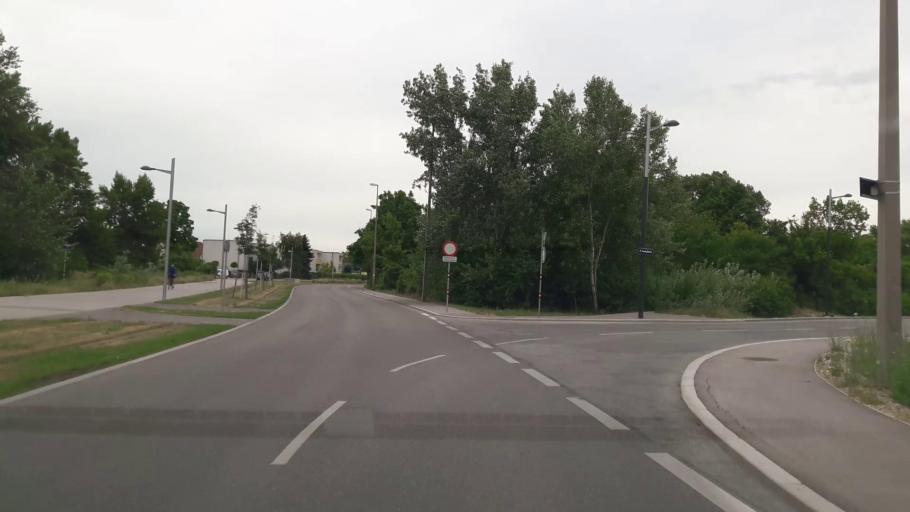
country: AT
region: Lower Austria
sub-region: Politischer Bezirk Ganserndorf
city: Gross-Enzersdorf
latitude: 48.2167
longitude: 16.5106
